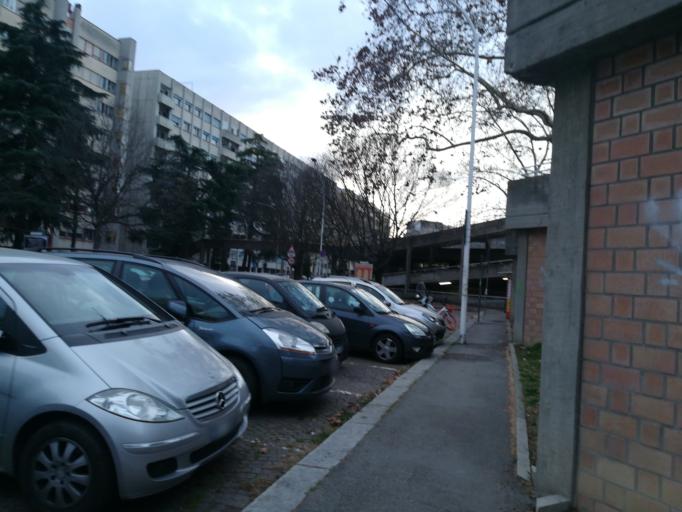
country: IT
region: Emilia-Romagna
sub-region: Provincia di Bologna
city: Progresso
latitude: 44.5459
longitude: 11.3596
